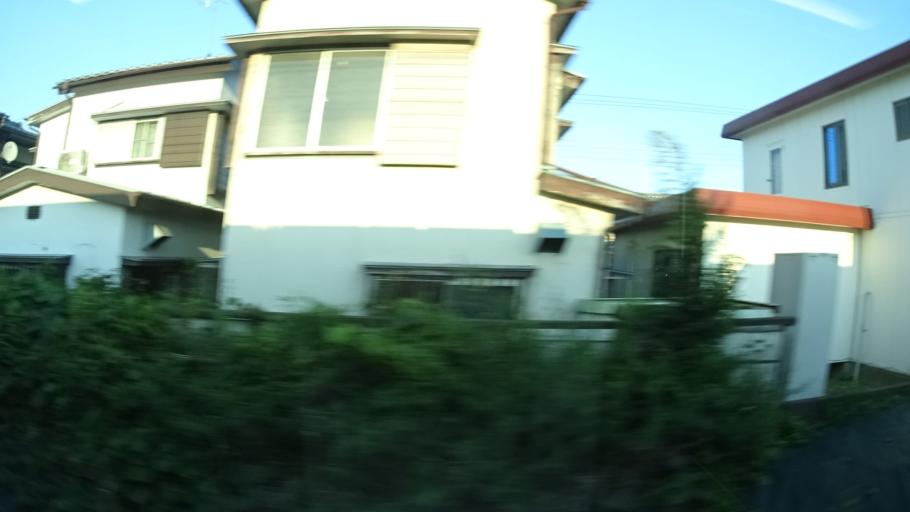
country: JP
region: Ibaraki
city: Ushiku
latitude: 35.9920
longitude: 140.1489
